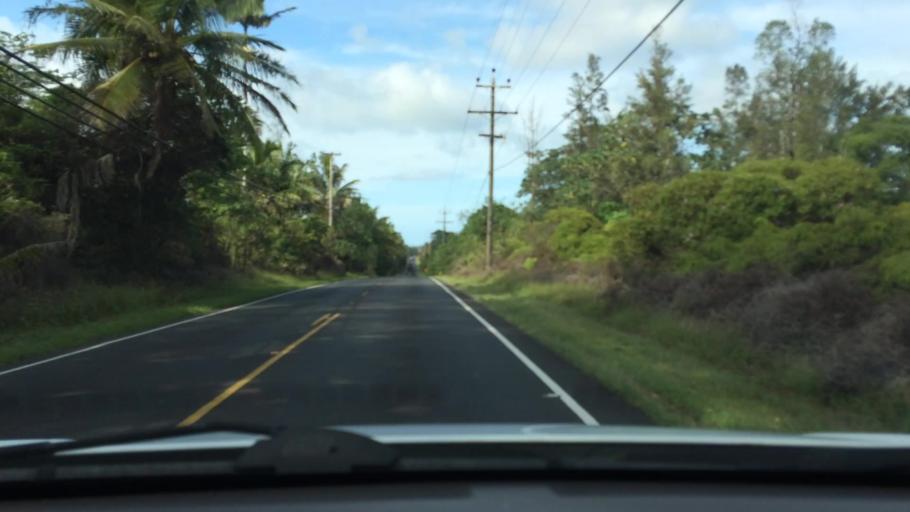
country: US
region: Hawaii
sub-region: Hawaii County
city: Hawaiian Paradise Park
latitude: 19.5111
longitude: -154.9441
